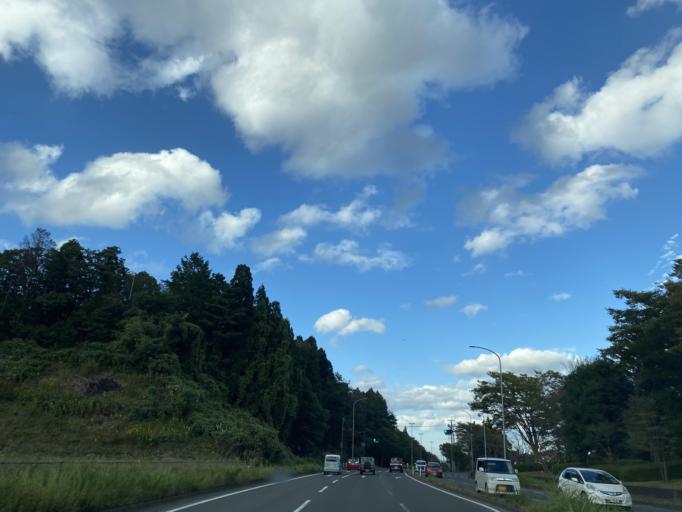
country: JP
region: Miyagi
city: Tomiya
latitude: 38.3544
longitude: 140.8432
